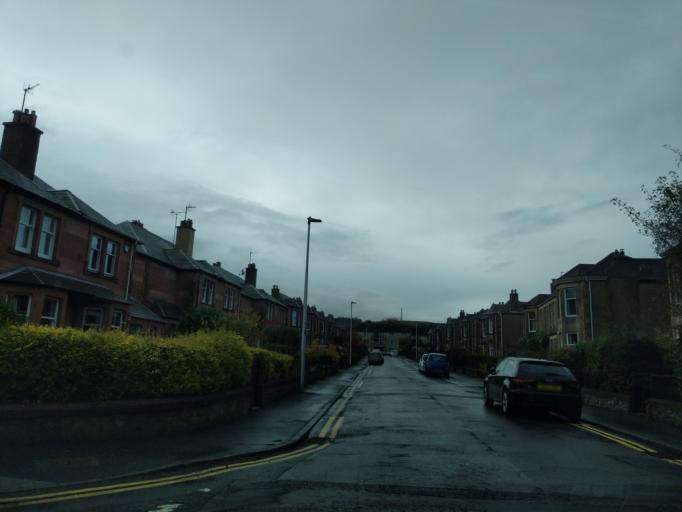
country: GB
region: Scotland
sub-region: Edinburgh
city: Edinburgh
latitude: 55.9285
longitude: -3.1773
